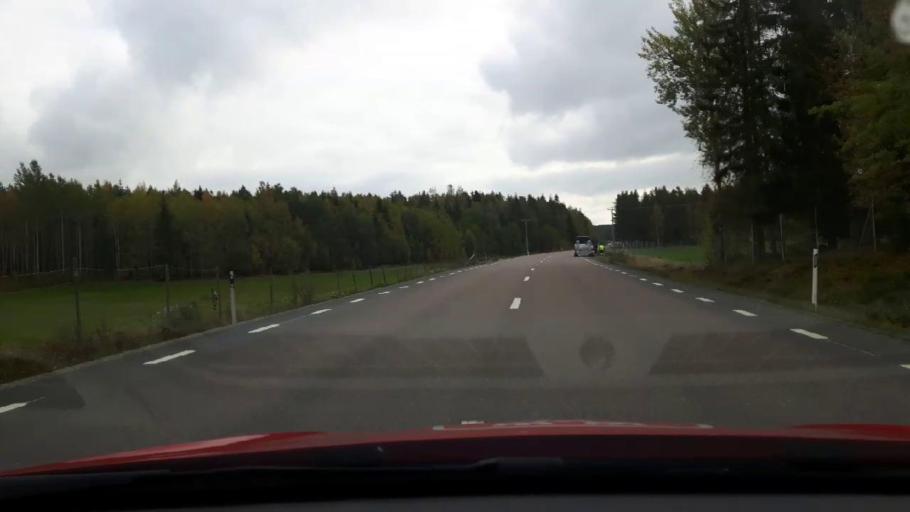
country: SE
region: Gaevleborg
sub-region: Bollnas Kommun
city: Bollnas
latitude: 61.3077
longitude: 16.4590
